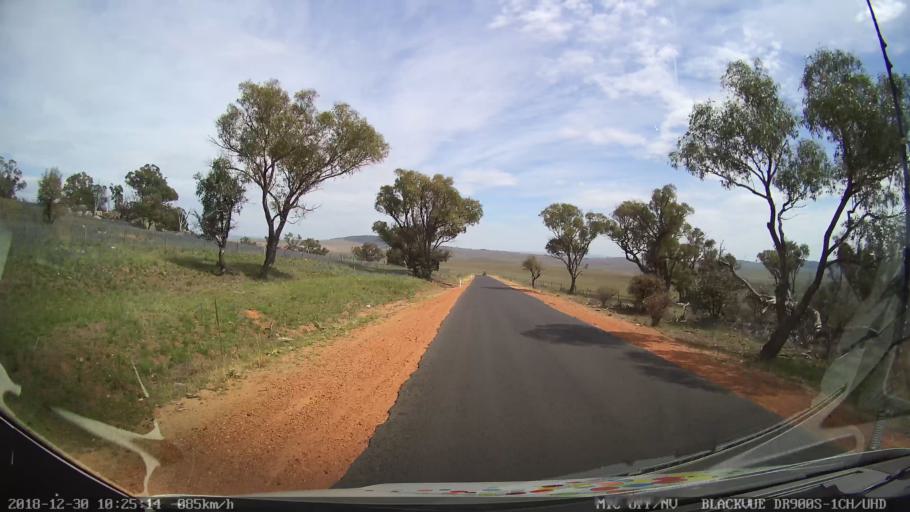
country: AU
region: New South Wales
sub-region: Snowy River
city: Berridale
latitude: -36.5266
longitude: 148.9604
